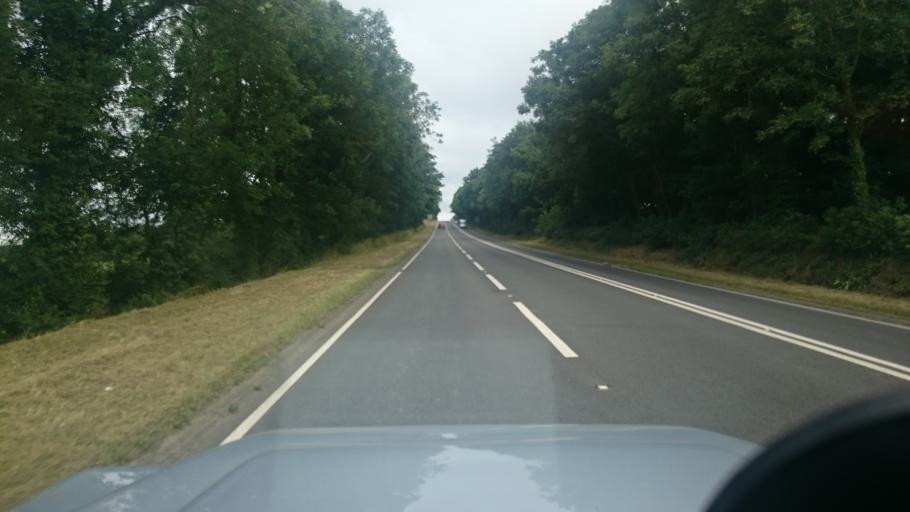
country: GB
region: Wales
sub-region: Pembrokeshire
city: Wiston
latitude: 51.8048
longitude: -4.8942
